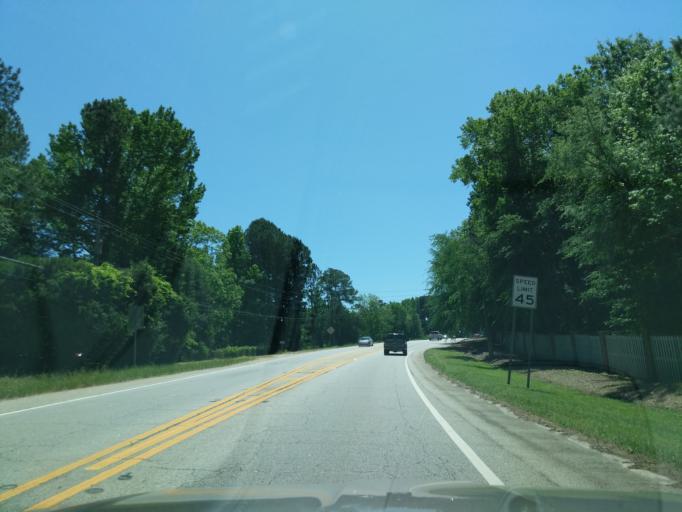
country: US
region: Georgia
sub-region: Columbia County
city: Martinez
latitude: 33.5547
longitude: -82.0933
